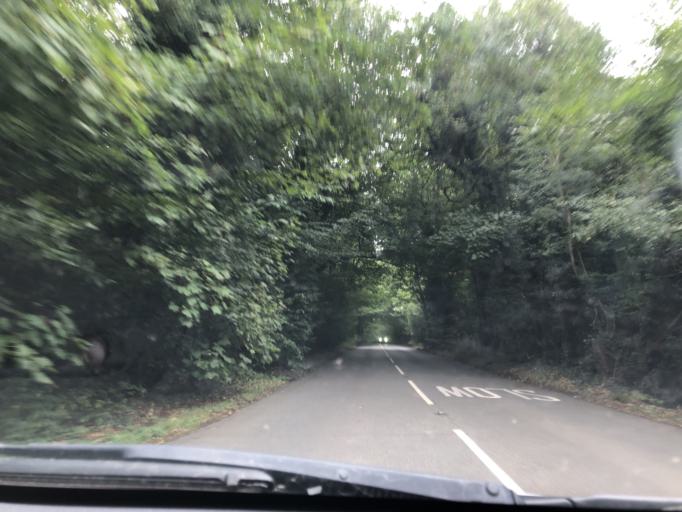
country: GB
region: England
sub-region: Kent
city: Westerham
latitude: 51.2582
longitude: 0.0800
